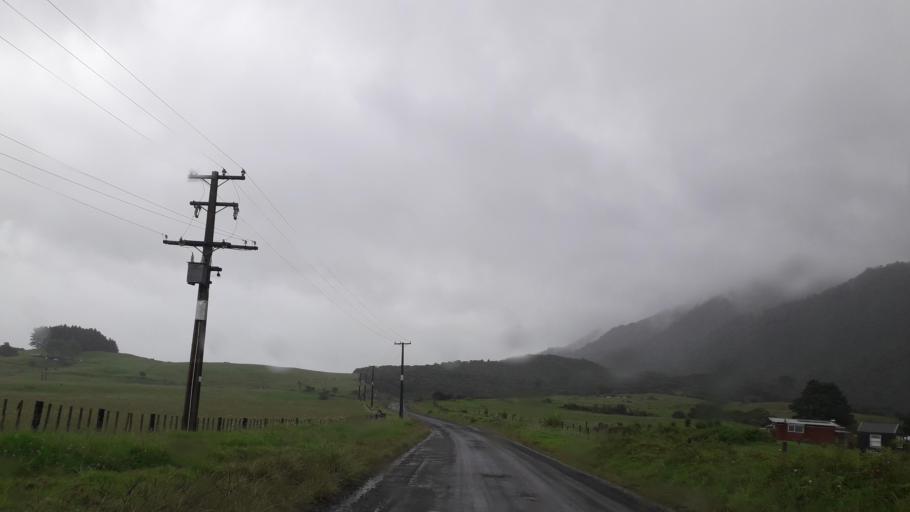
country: NZ
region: Northland
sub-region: Far North District
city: Kaitaia
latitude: -35.4046
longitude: 173.3676
